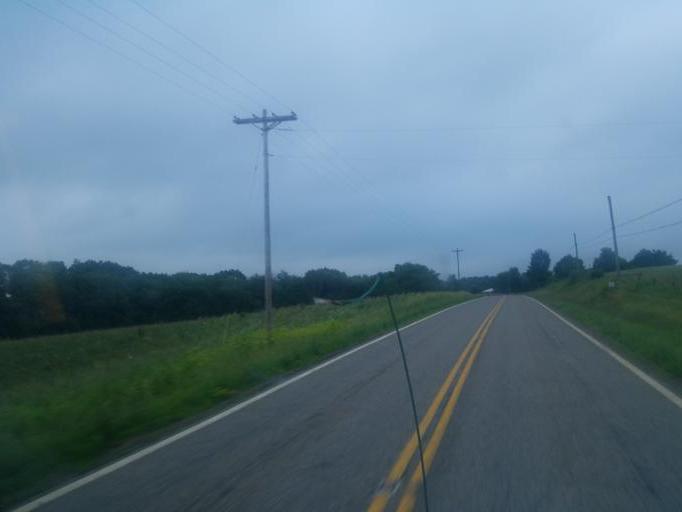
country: US
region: Ohio
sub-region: Columbiana County
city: Salineville
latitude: 40.6207
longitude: -80.9054
